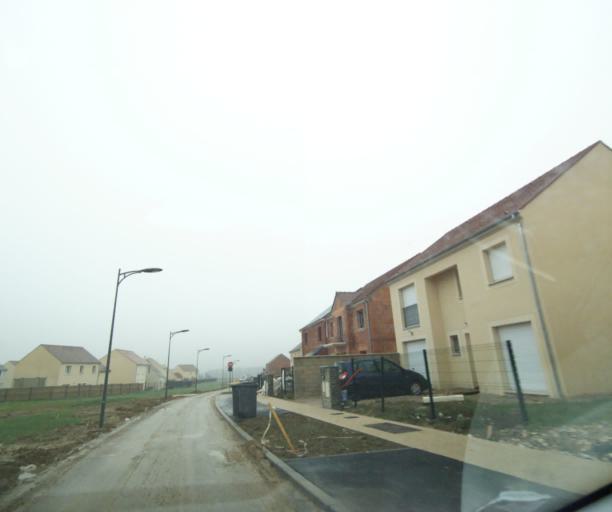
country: FR
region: Ile-de-France
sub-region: Departement de Seine-et-Marne
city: Dammartin-en-Goele
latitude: 49.0616
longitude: 2.6723
